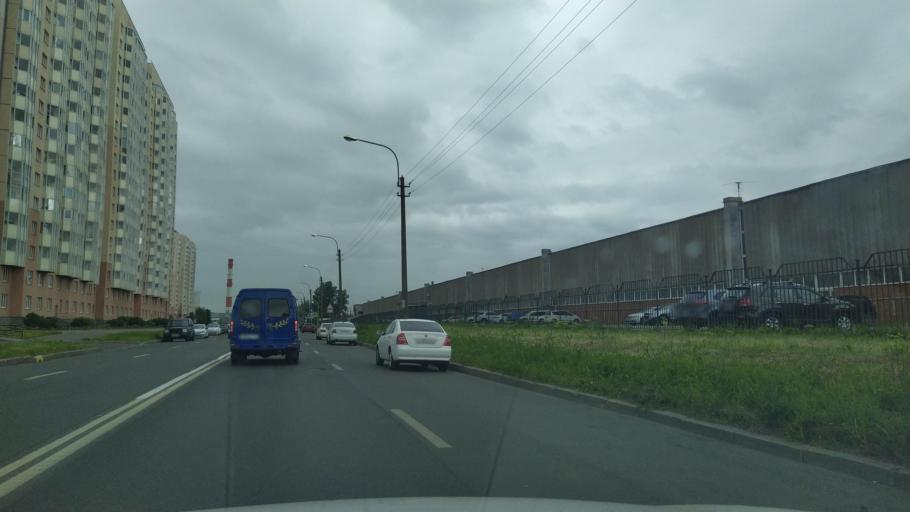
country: RU
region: St.-Petersburg
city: Kupchino
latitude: 59.8374
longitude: 30.3109
